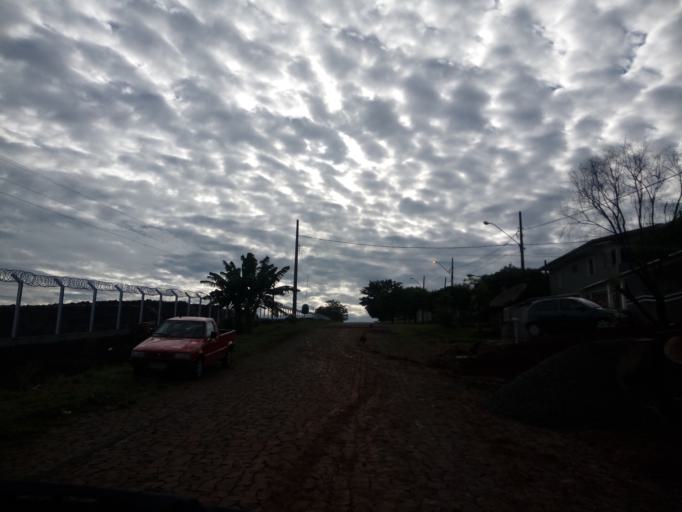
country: BR
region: Santa Catarina
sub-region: Chapeco
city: Chapeco
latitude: -27.1072
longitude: -52.6337
